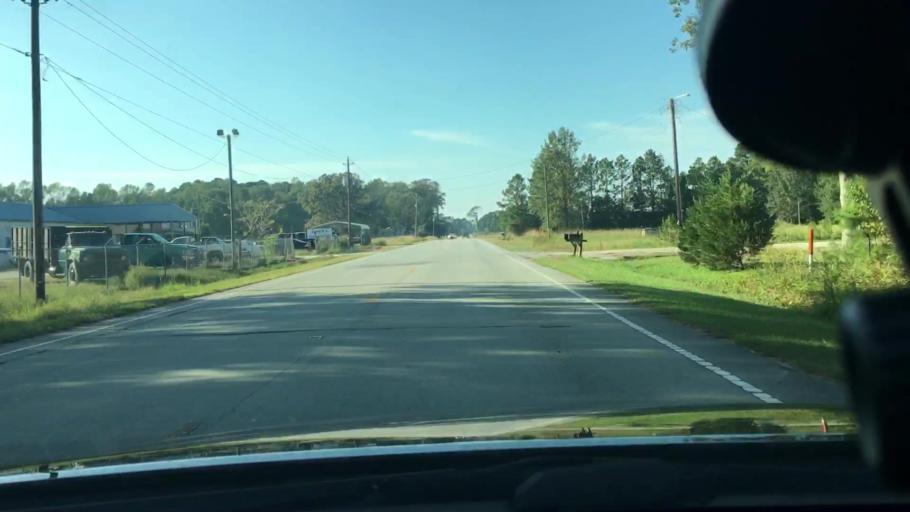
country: US
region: North Carolina
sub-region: Craven County
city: Vanceboro
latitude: 35.3484
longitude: -77.1853
